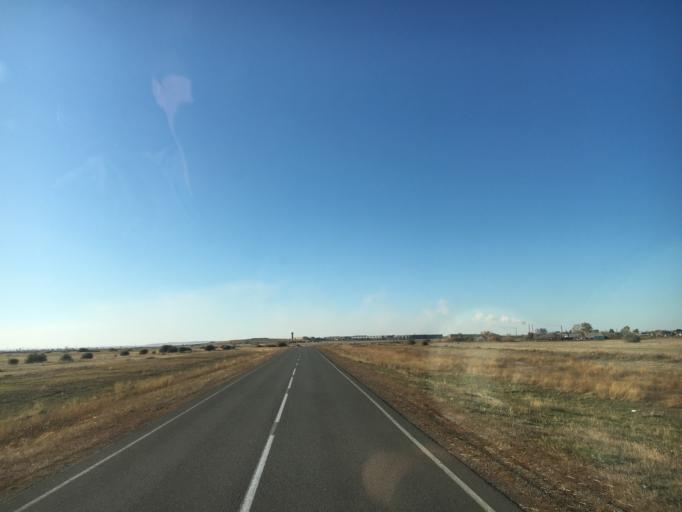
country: KZ
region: Qaraghandy
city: Aqtau
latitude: 50.1967
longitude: 73.0894
